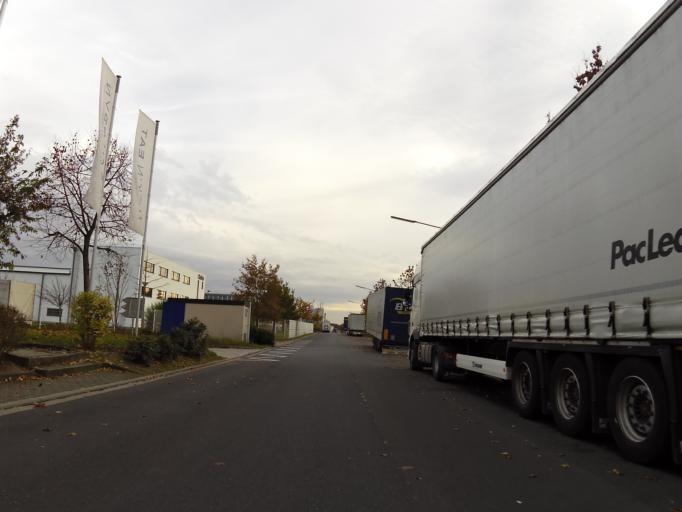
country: DE
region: Hesse
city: Morfelden-Walldorf
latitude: 49.9888
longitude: 8.5840
